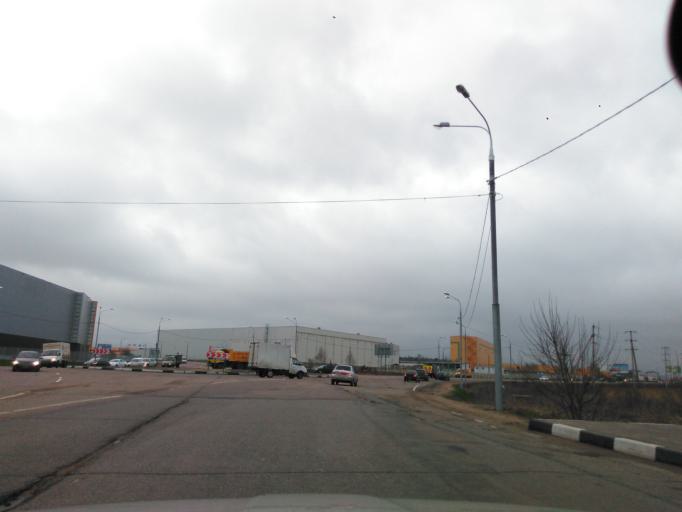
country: RU
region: Moskovskaya
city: Pavlovskaya Sloboda
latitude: 55.8126
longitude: 37.1103
